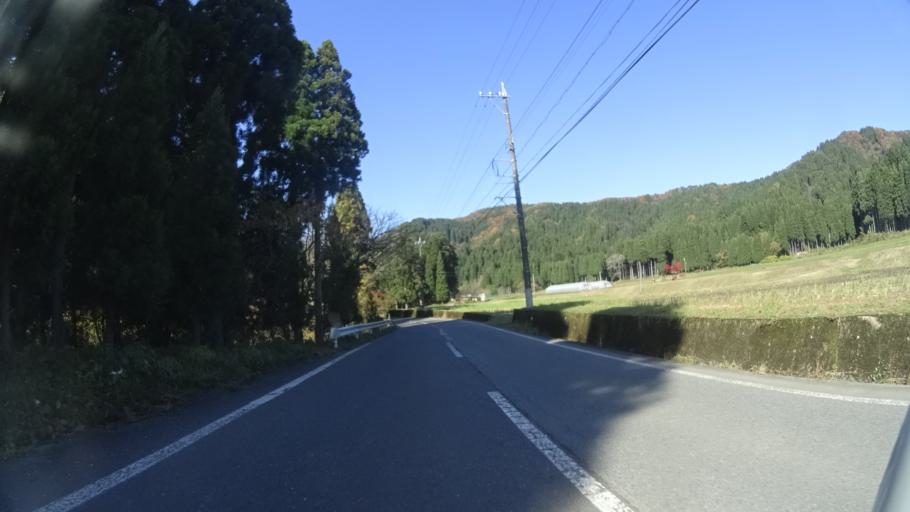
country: JP
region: Fukui
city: Ono
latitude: 35.8749
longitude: 136.3574
